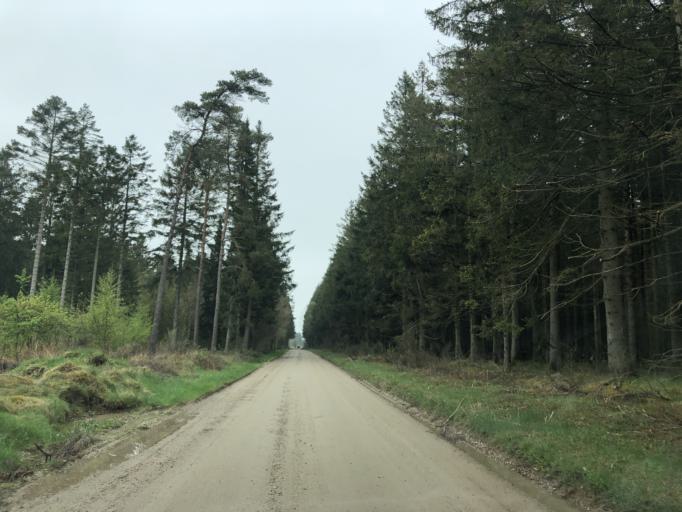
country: DK
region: Central Jutland
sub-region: Lemvig Kommune
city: Lemvig
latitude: 56.4995
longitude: 8.3349
